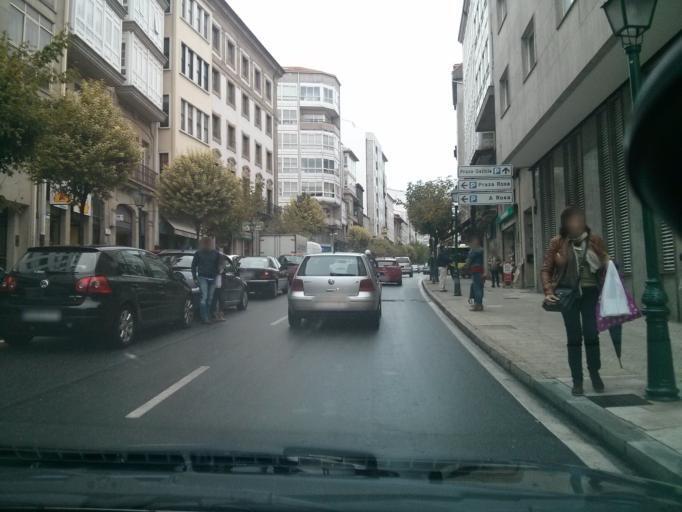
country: ES
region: Galicia
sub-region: Provincia da Coruna
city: Santiago de Compostela
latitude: 42.8740
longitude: -8.5447
